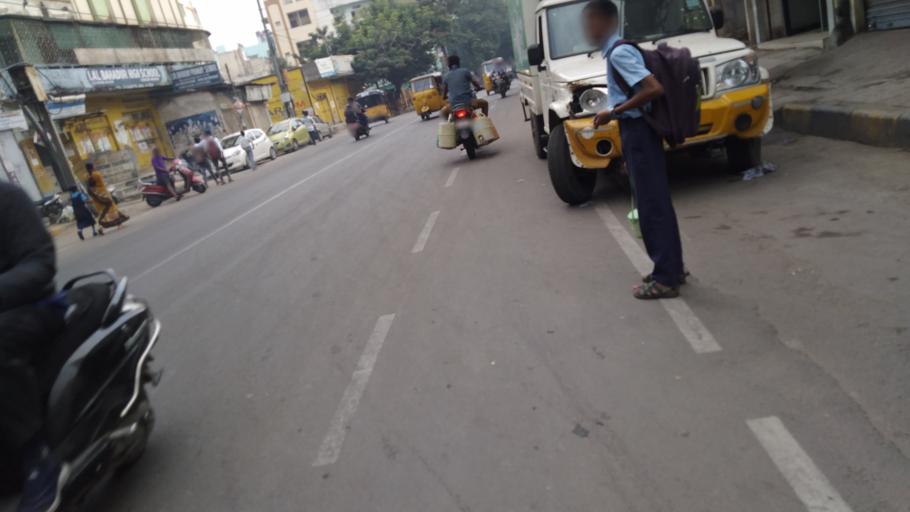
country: IN
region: Telangana
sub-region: Rangareddi
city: Gaddi Annaram
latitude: 17.3855
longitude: 78.4941
